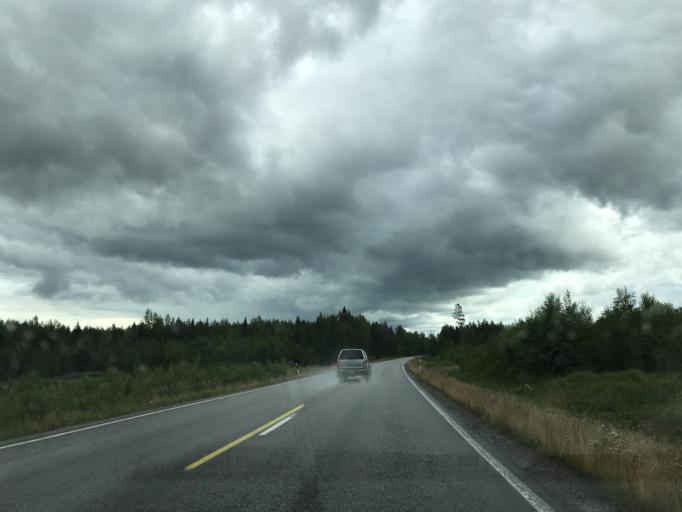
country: FI
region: Uusimaa
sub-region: Porvoo
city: Pukkila
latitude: 60.7699
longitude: 25.5244
